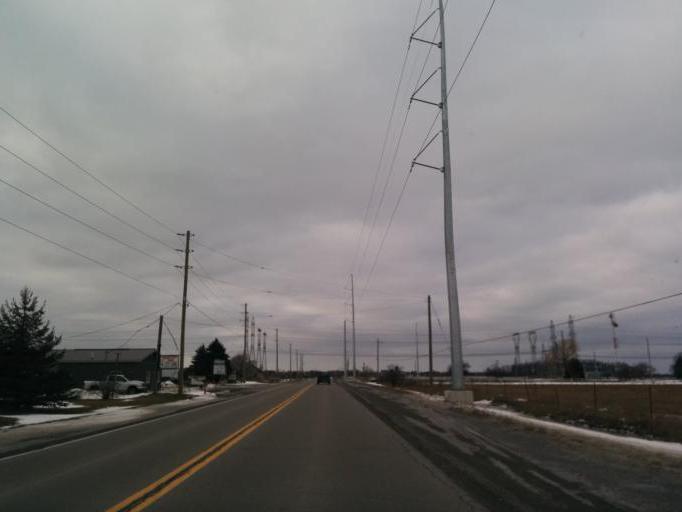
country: CA
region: Ontario
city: Ancaster
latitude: 42.9517
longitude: -80.0230
